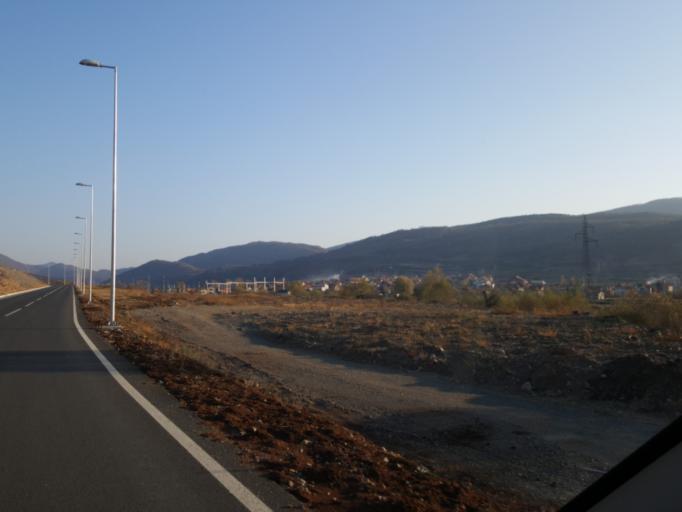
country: RS
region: Central Serbia
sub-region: Pirotski Okrug
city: Dimitrovgrad
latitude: 43.0170
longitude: 22.7487
